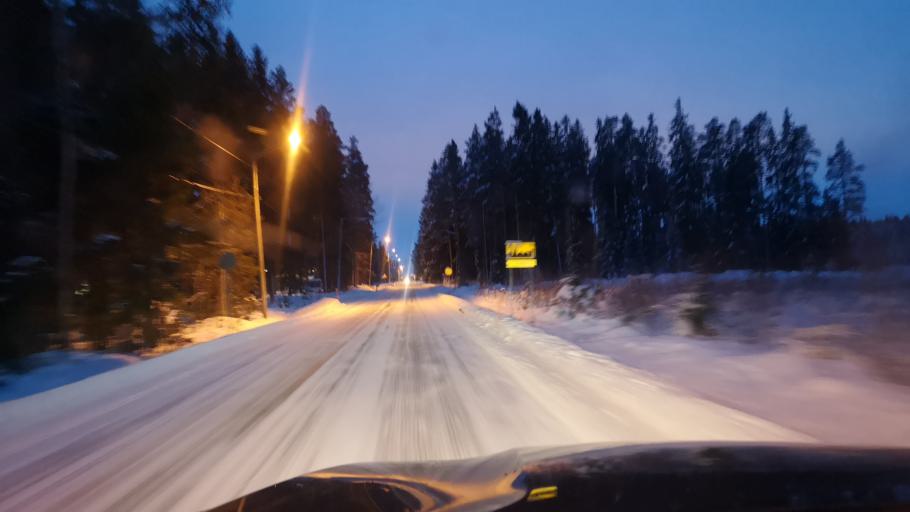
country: FI
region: Varsinais-Suomi
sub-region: Loimaa
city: Loimaa
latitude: 60.8689
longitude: 23.0883
